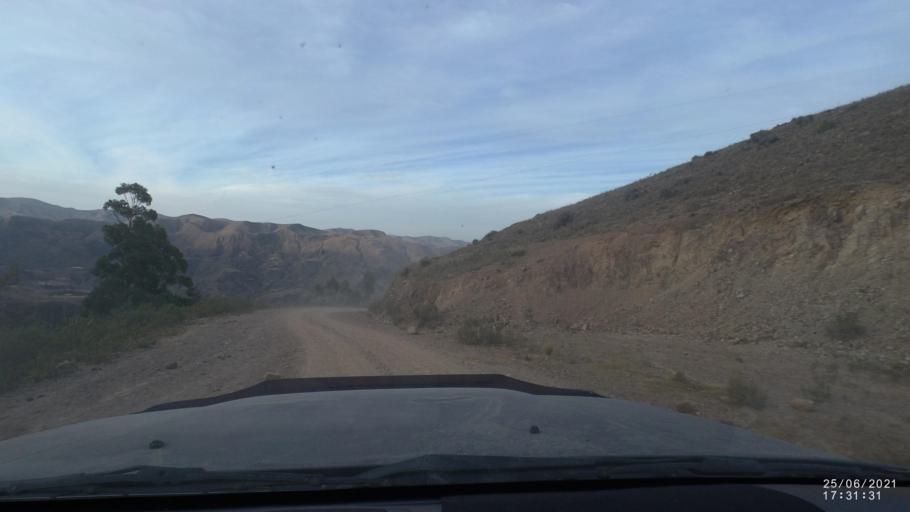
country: BO
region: Cochabamba
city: Mizque
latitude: -17.9375
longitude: -65.6643
